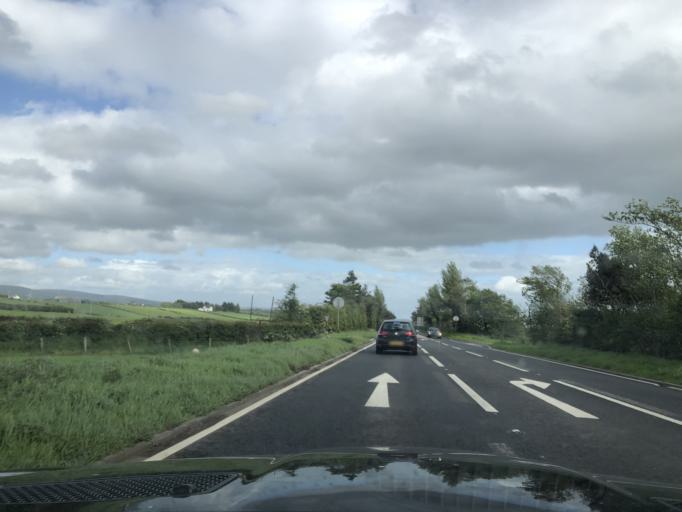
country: GB
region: Northern Ireland
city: Dunloy
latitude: 55.0368
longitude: -6.4099
